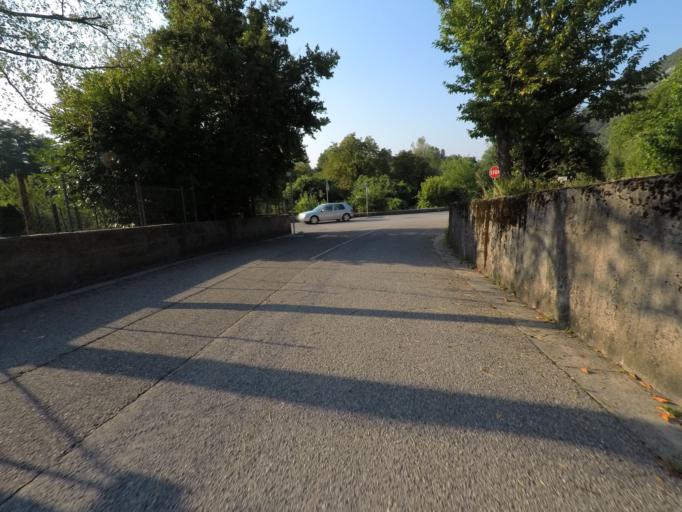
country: IT
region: Friuli Venezia Giulia
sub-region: Provincia di Udine
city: Trasaghis
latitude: 46.2559
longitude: 13.0381
